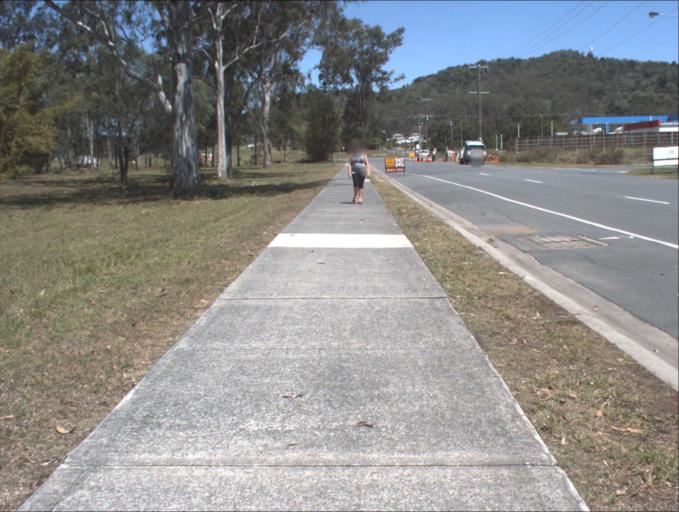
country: AU
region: Queensland
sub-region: Logan
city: Windaroo
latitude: -27.7535
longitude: 153.1889
